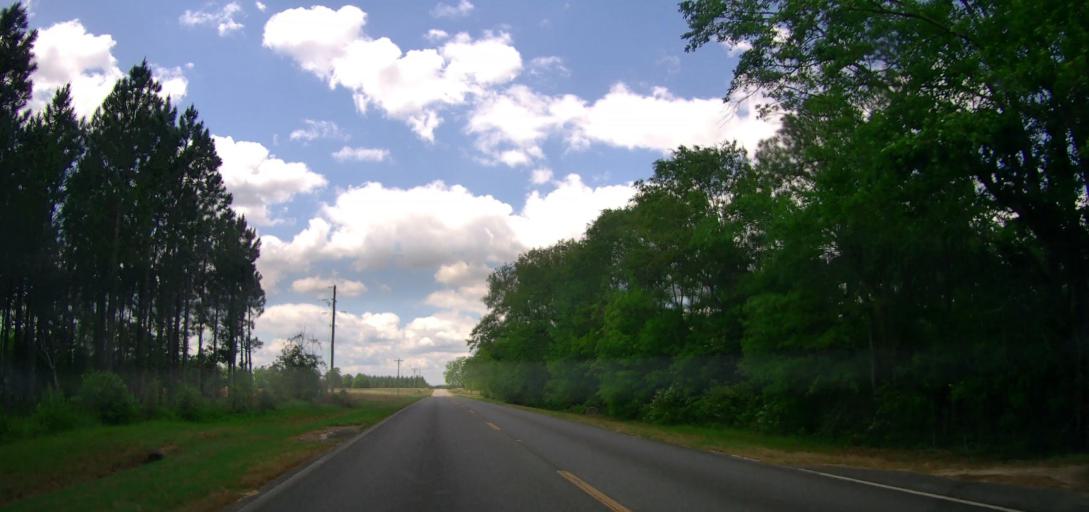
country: US
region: Georgia
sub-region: Treutlen County
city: Soperton
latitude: 32.5266
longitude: -82.6841
